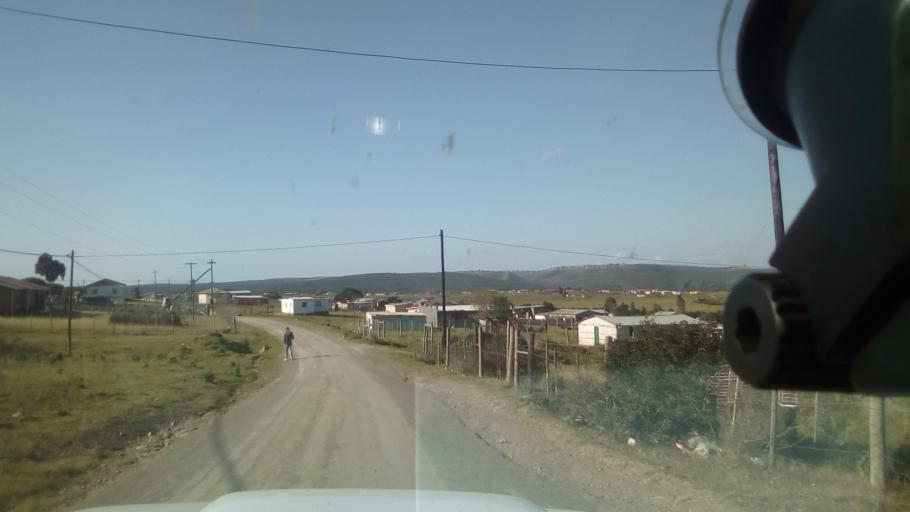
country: ZA
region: Eastern Cape
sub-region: Buffalo City Metropolitan Municipality
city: Bhisho
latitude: -32.8136
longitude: 27.3544
